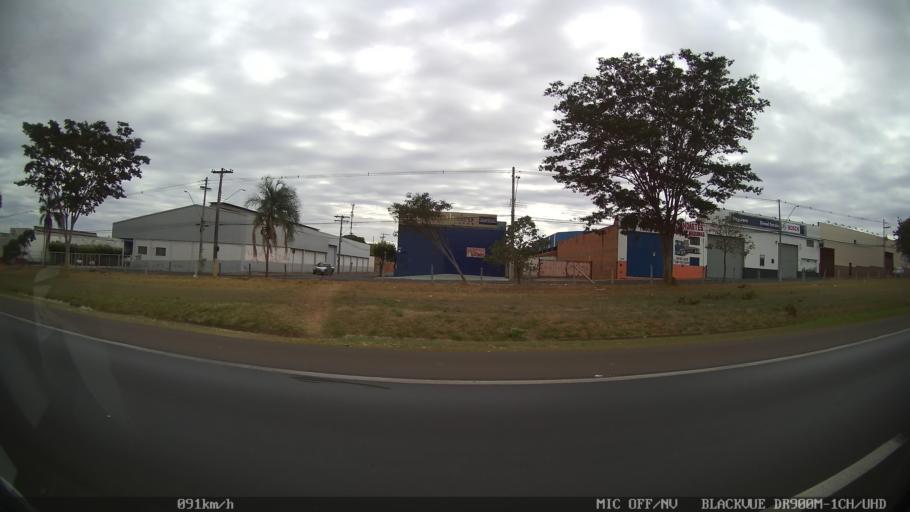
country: BR
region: Sao Paulo
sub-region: Sao Jose Do Rio Preto
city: Sao Jose do Rio Preto
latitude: -20.8096
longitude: -49.4974
